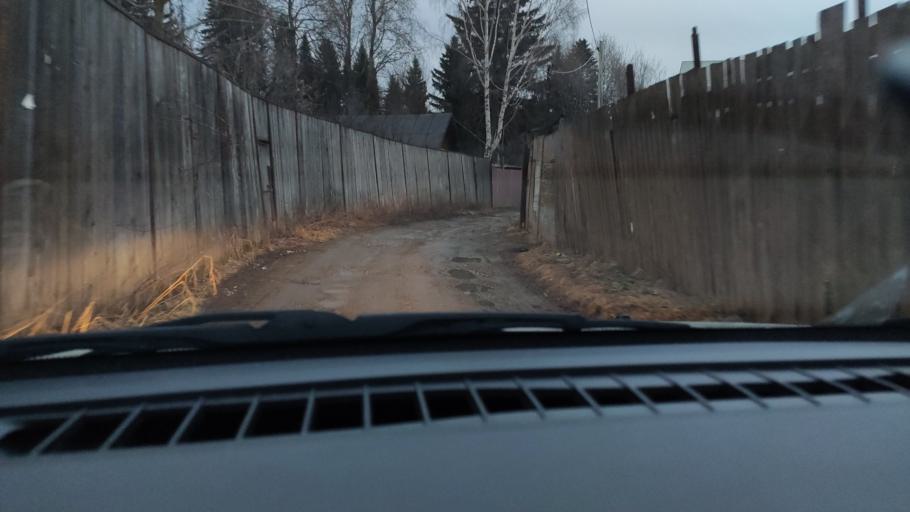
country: RU
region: Perm
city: Polazna
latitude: 58.1806
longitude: 56.4165
